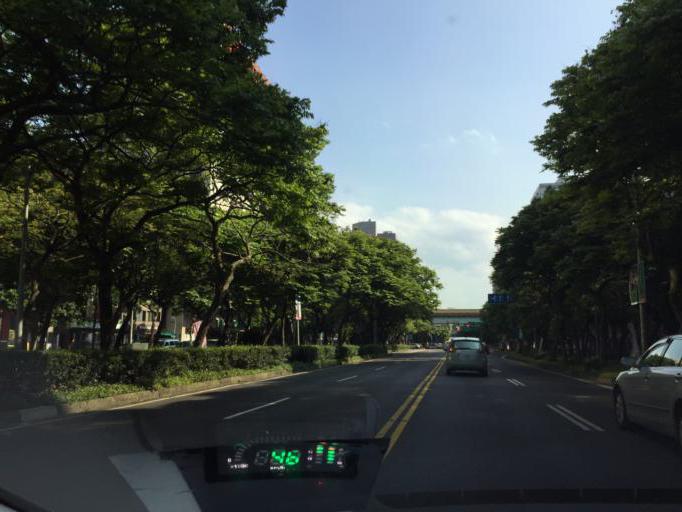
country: TW
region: Taipei
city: Taipei
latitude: 25.0264
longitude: 121.5488
